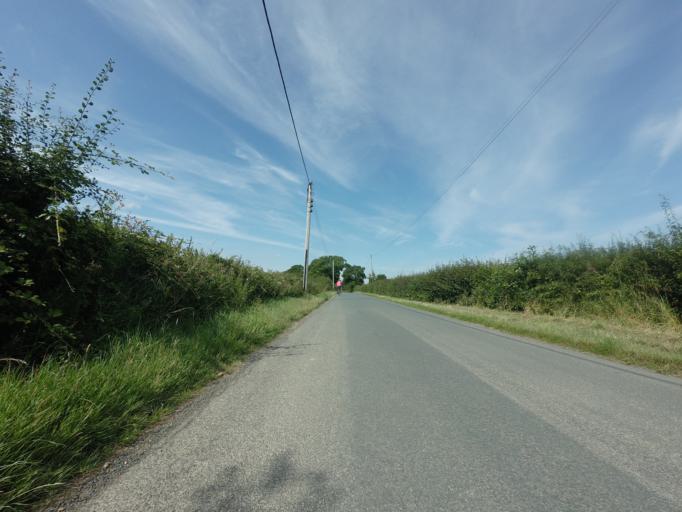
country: GB
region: England
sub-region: East Sussex
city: Rye
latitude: 50.9753
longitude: 0.7397
